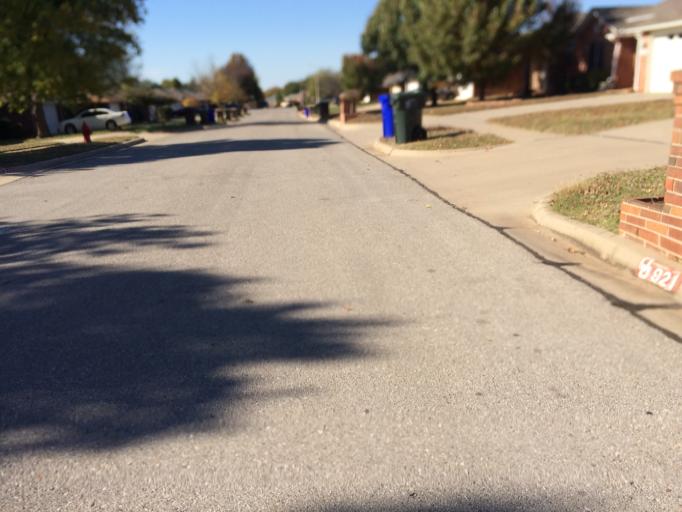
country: US
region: Oklahoma
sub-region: Cleveland County
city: Noble
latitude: 35.1703
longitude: -97.4274
